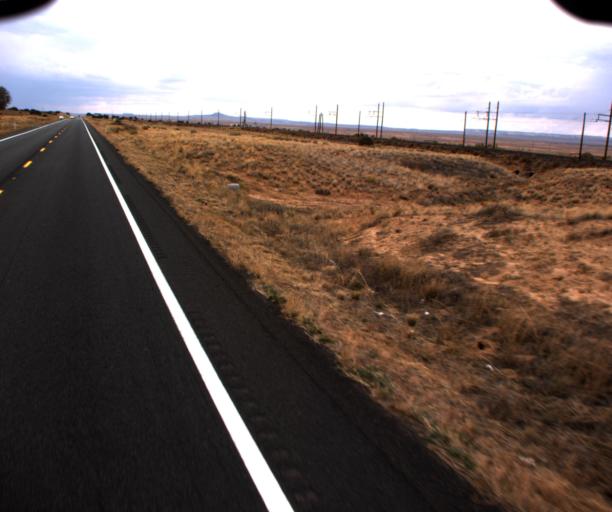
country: US
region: Arizona
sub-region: Coconino County
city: Kaibito
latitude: 36.4140
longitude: -110.8189
